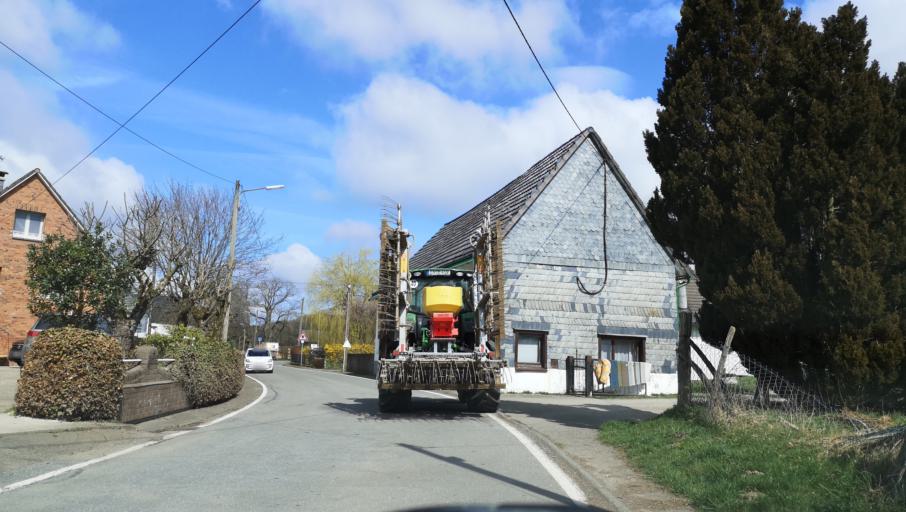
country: DE
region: North Rhine-Westphalia
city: Radevormwald
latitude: 51.2429
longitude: 7.3934
